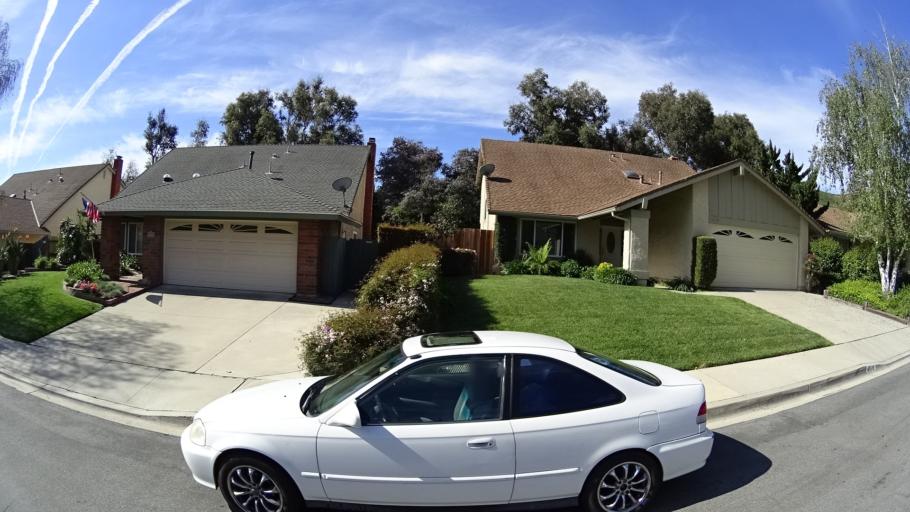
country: US
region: California
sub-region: Ventura County
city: Casa Conejo
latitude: 34.1804
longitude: -118.9601
